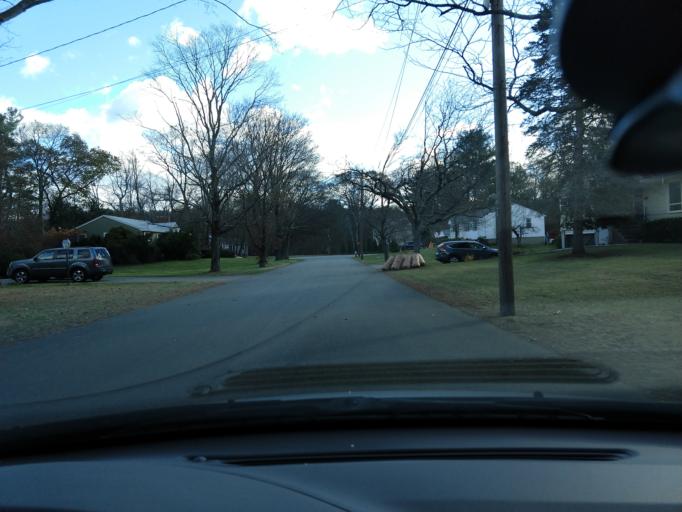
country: US
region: Massachusetts
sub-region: Middlesex County
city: Bedford
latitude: 42.4903
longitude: -71.2607
